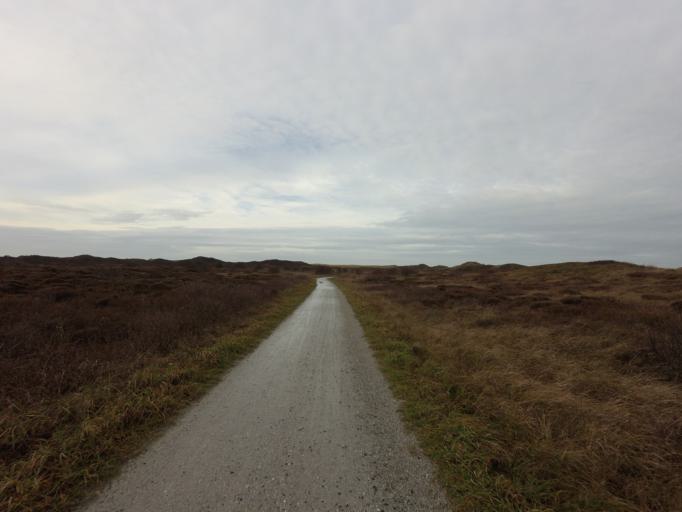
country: NL
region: North Holland
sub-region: Gemeente Texel
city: Den Burg
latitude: 53.0613
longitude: 4.7326
